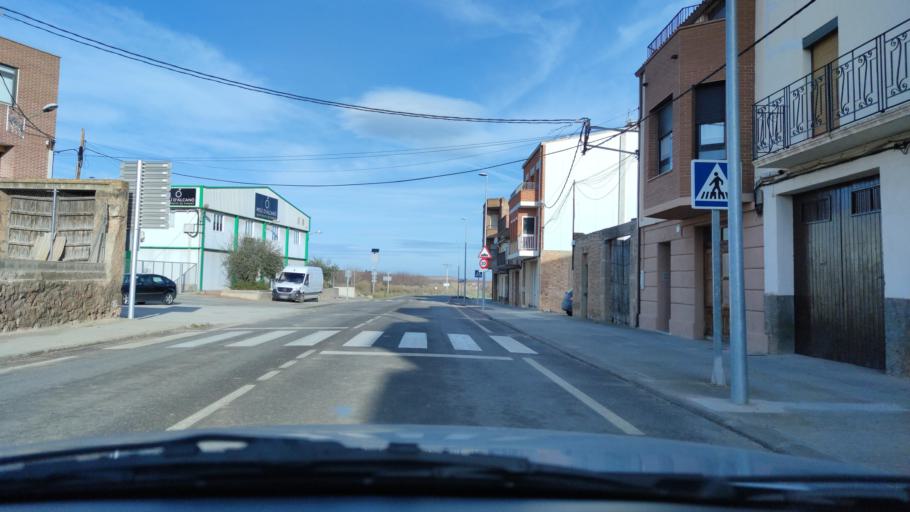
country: ES
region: Catalonia
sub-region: Provincia de Lleida
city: Alcano
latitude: 41.4827
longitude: 0.6167
